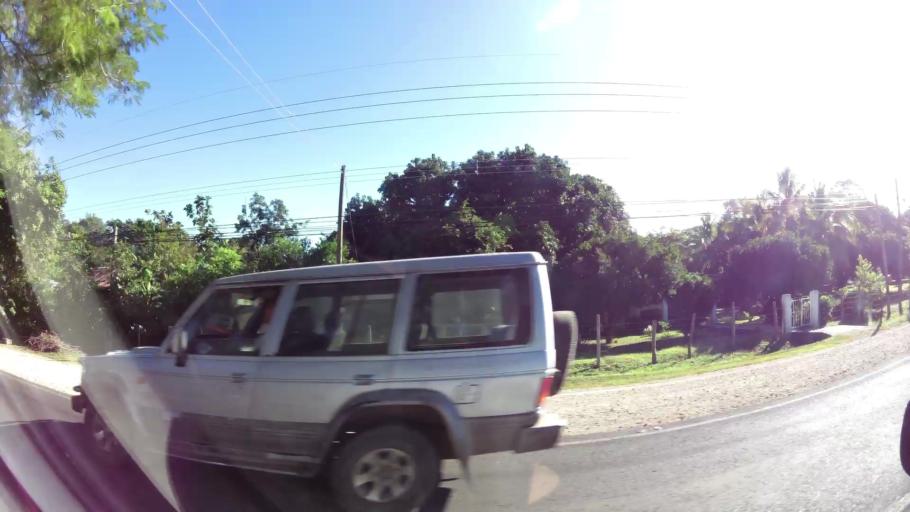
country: CR
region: Guanacaste
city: Belen
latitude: 10.4614
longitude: -85.5585
